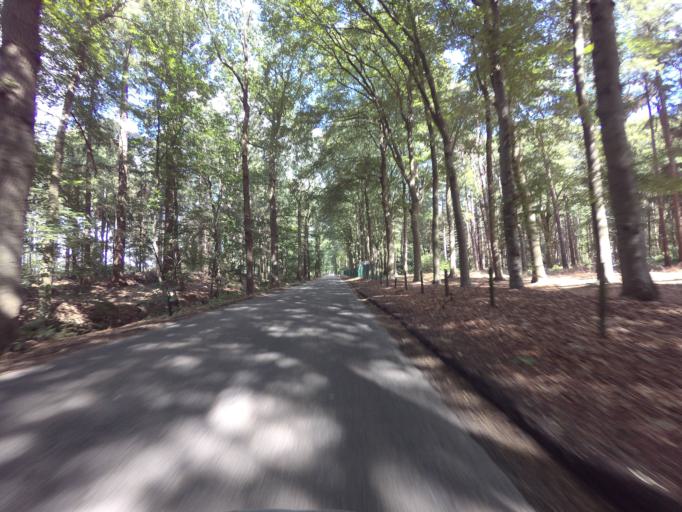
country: NL
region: Utrecht
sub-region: Gemeente Soest
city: Soest
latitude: 52.1667
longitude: 5.2306
